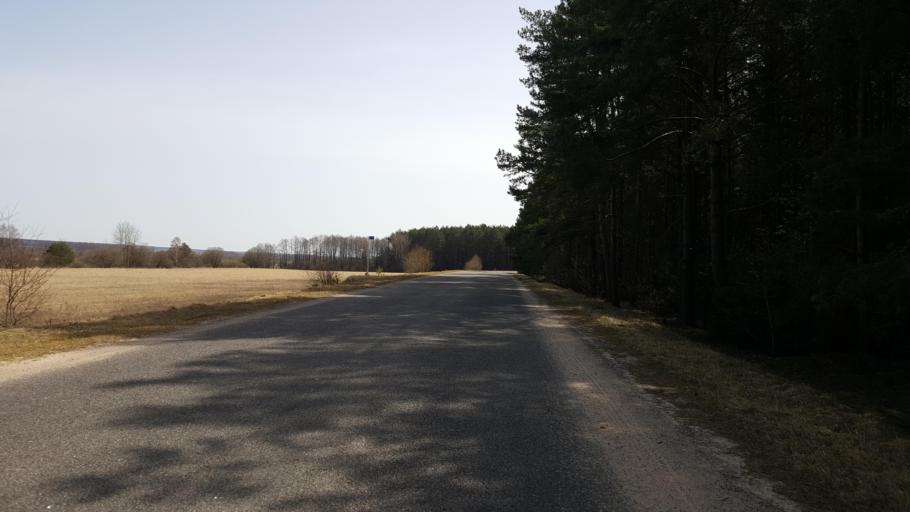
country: BY
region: Brest
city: Kamyanyuki
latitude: 52.5178
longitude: 23.8512
